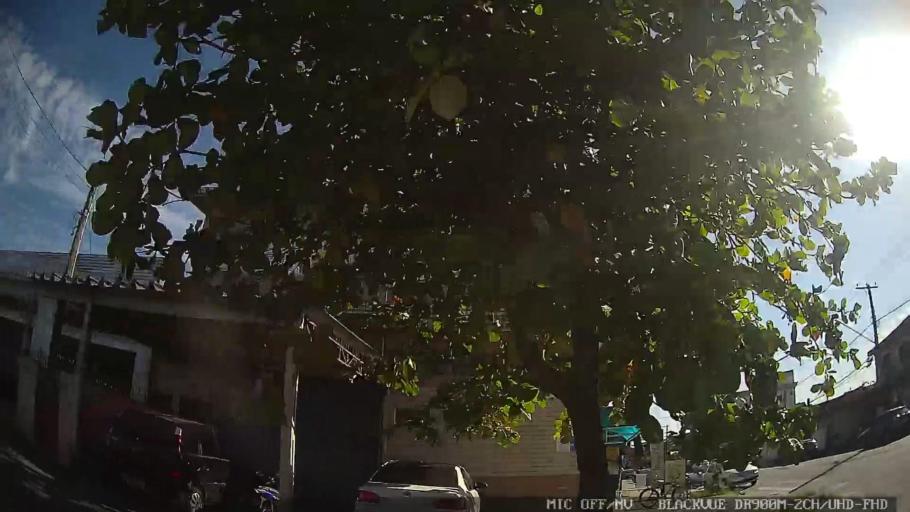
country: BR
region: Sao Paulo
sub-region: Santos
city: Santos
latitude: -23.9546
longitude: -46.2898
